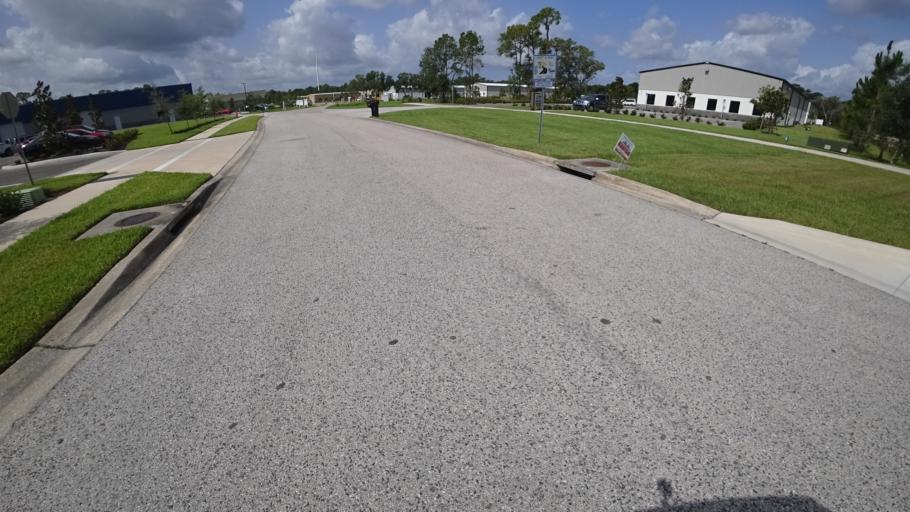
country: US
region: Florida
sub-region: Manatee County
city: Samoset
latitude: 27.4570
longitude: -82.4557
